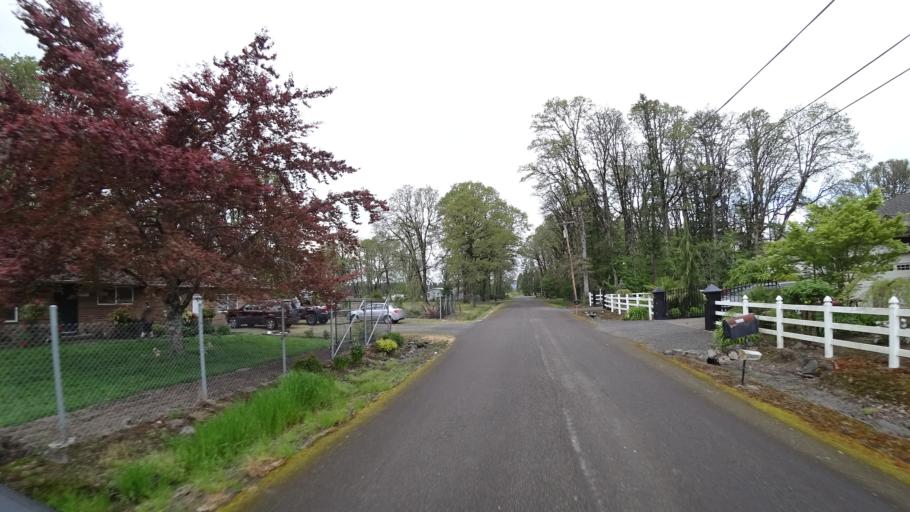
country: US
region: Oregon
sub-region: Washington County
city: Hillsboro
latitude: 45.5556
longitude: -122.9584
